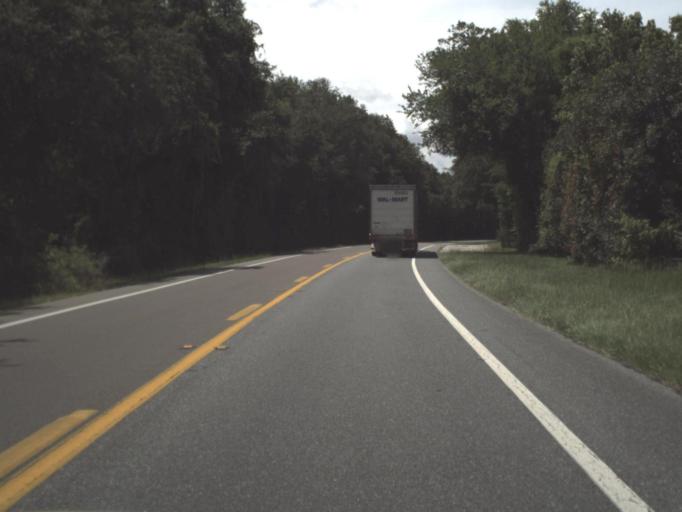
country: US
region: Florida
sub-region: Alachua County
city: Newberry
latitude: 29.6173
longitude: -82.5952
